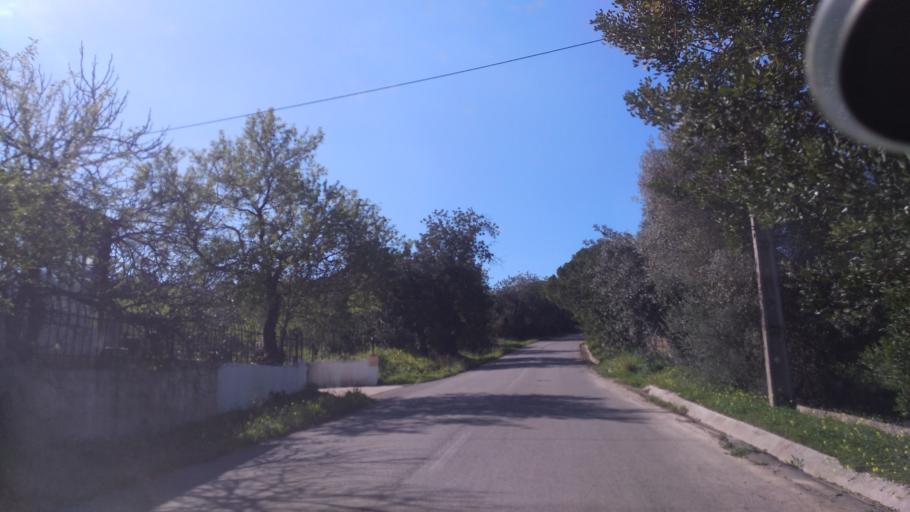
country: PT
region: Faro
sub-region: Faro
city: Santa Barbara de Nexe
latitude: 37.1164
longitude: -7.9291
